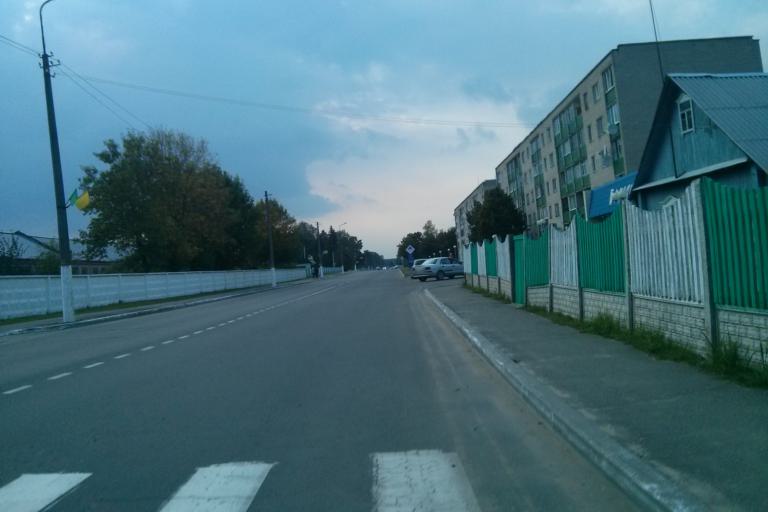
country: BY
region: Minsk
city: Chervyen'
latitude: 53.7188
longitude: 28.4007
